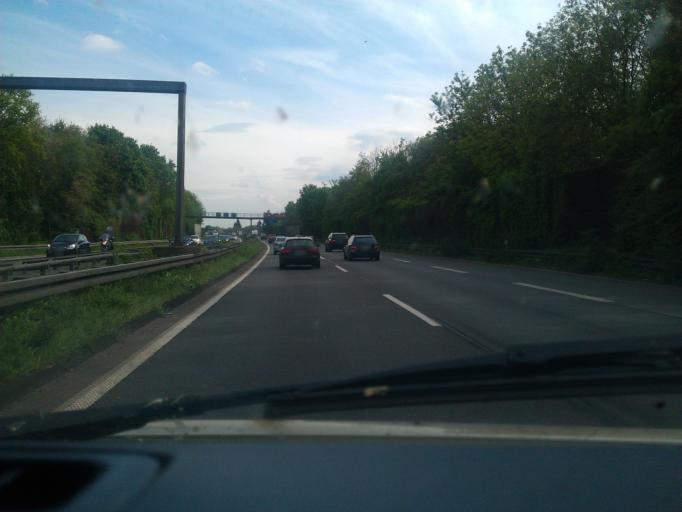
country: DE
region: North Rhine-Westphalia
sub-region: Regierungsbezirk Dusseldorf
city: Krefeld
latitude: 51.3396
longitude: 6.6245
